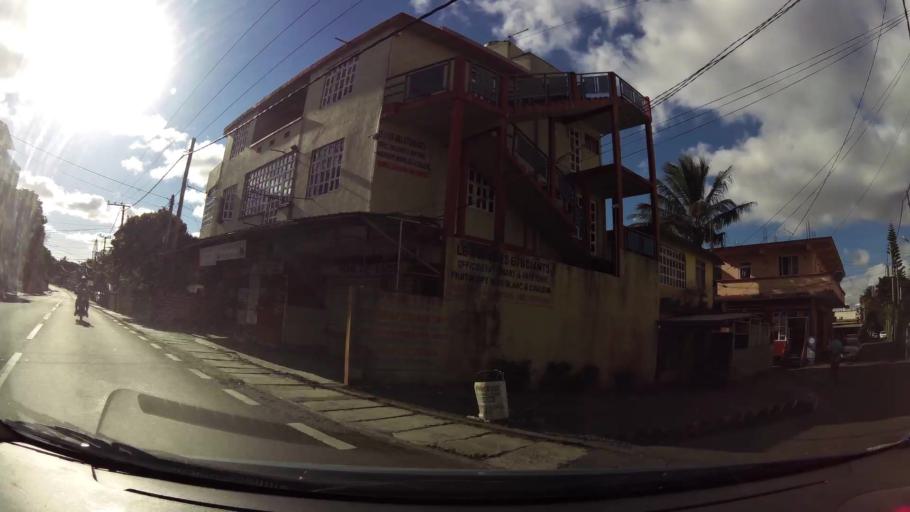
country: MU
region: Plaines Wilhems
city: Curepipe
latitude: -20.2932
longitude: 57.5177
